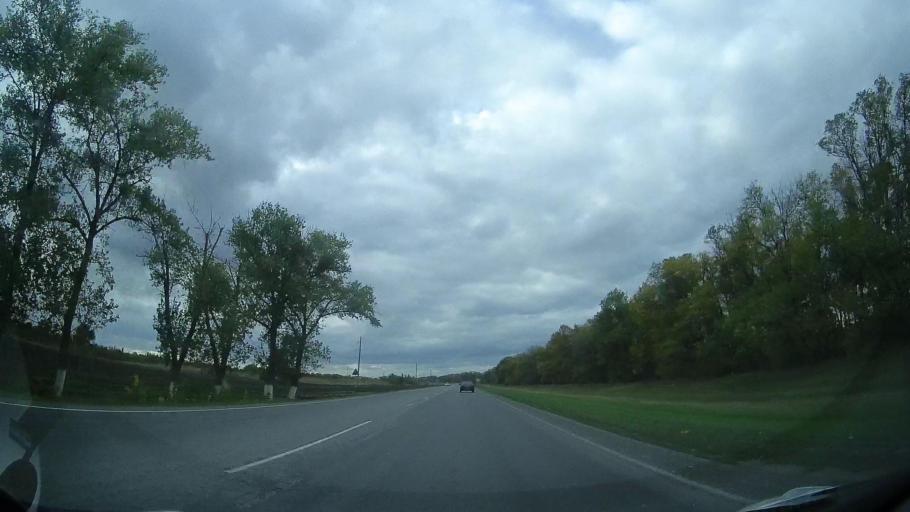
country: RU
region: Rostov
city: Zernograd
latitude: 46.8007
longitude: 40.3605
